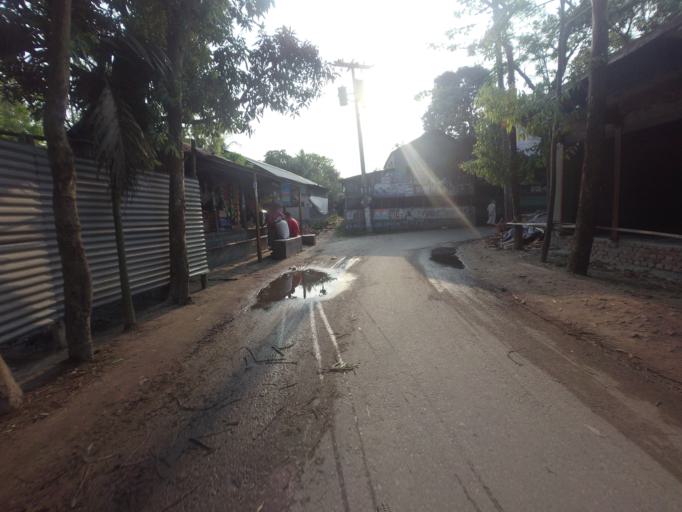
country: BD
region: Rajshahi
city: Sirajganj
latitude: 24.3183
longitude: 89.6956
